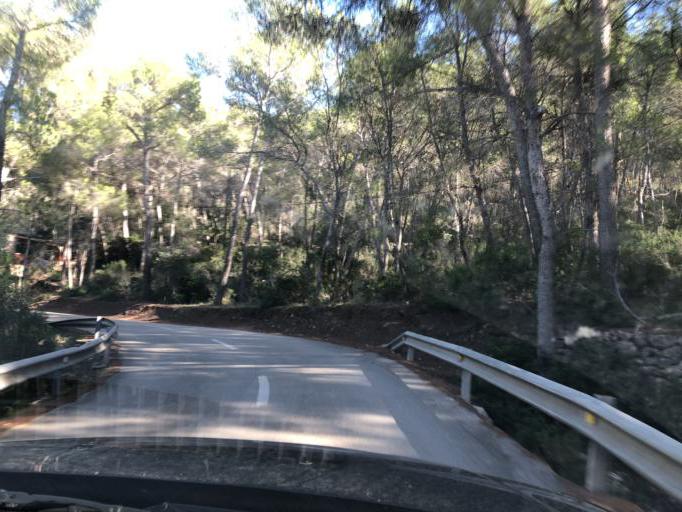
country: ES
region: Balearic Islands
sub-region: Illes Balears
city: Camp de Mar
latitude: 39.5415
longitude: 2.3977
